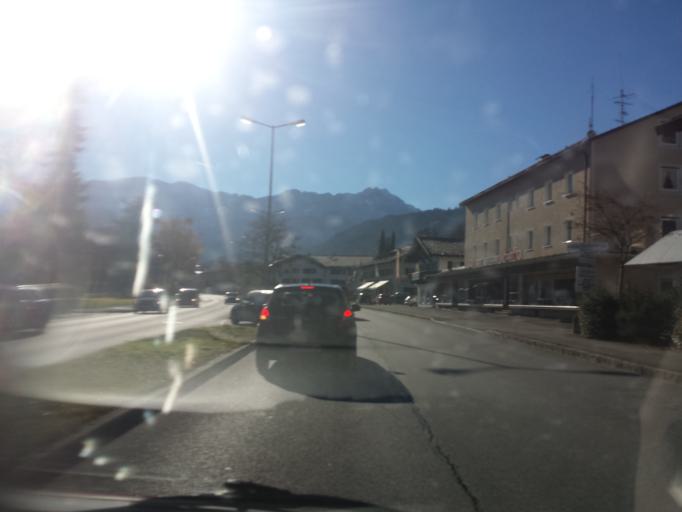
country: DE
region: Bavaria
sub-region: Upper Bavaria
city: Garmisch-Partenkirchen
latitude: 47.4985
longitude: 11.1012
